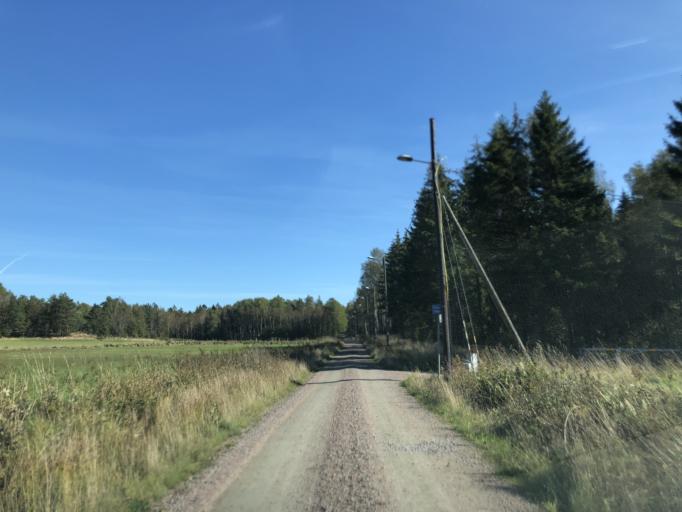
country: SE
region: Vaestra Goetaland
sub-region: Goteborg
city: Majorna
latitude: 57.7656
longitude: 11.9094
